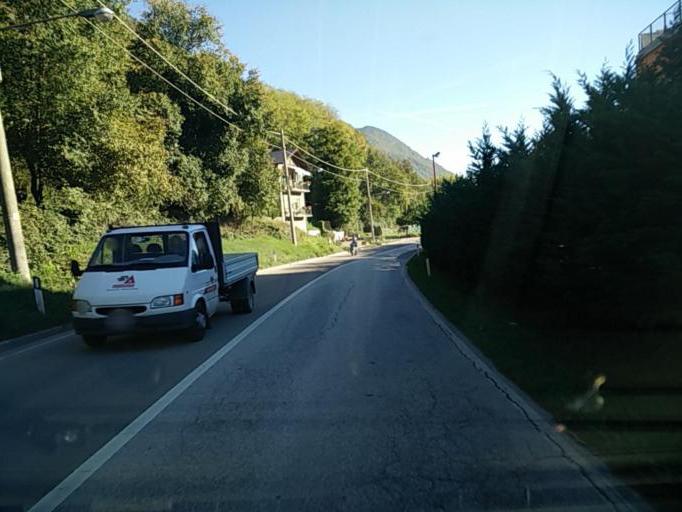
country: IT
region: Trentino-Alto Adige
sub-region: Bolzano
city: Sinigo
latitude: 46.6262
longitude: 11.1842
